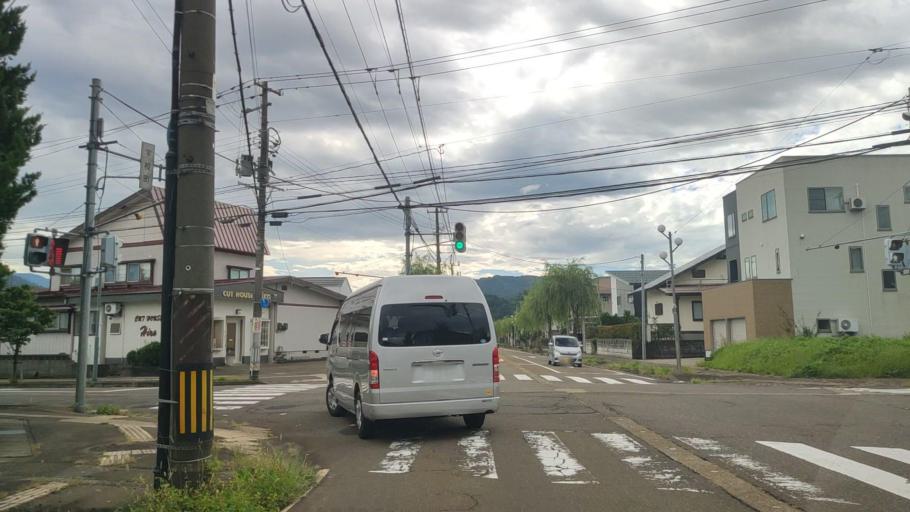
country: JP
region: Niigata
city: Arai
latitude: 37.0196
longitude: 138.2474
